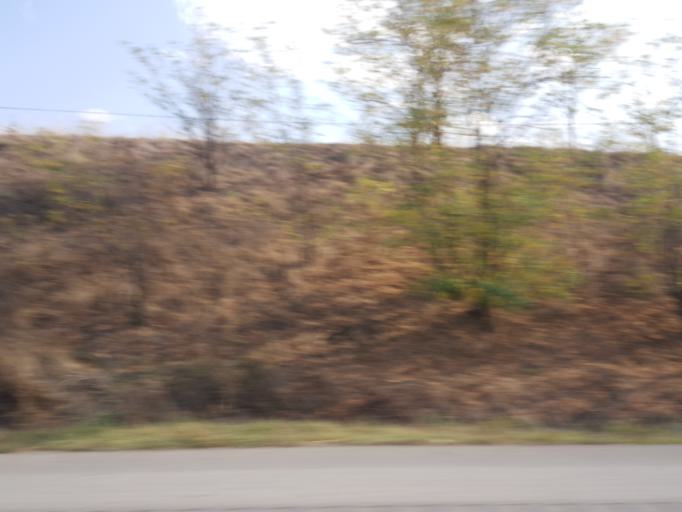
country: TR
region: Corum
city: Seydim
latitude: 40.4429
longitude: 34.8208
